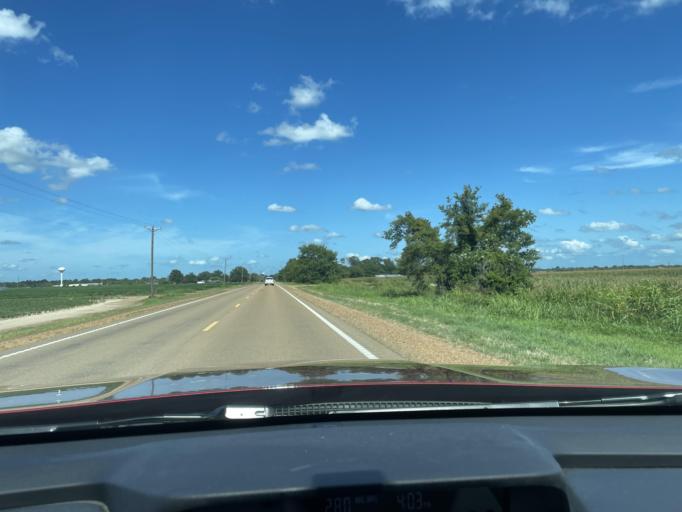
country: US
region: Mississippi
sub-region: Humphreys County
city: Belzoni
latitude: 33.1838
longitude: -90.5112
